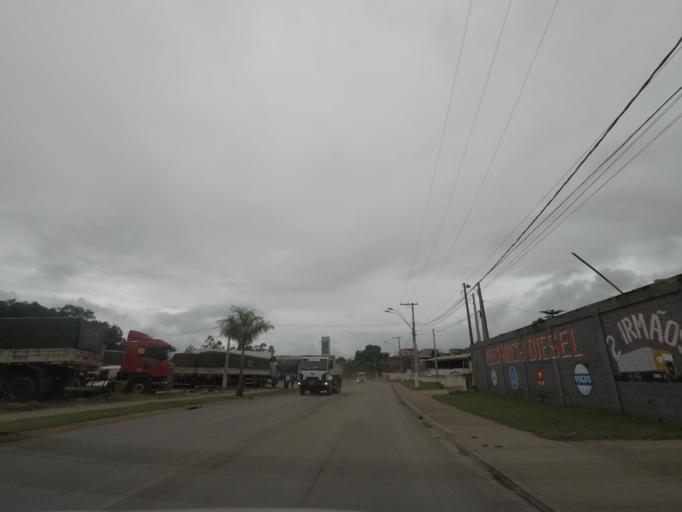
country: BR
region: Sao Paulo
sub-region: Cajati
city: Cajati
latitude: -24.7214
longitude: -48.0997
